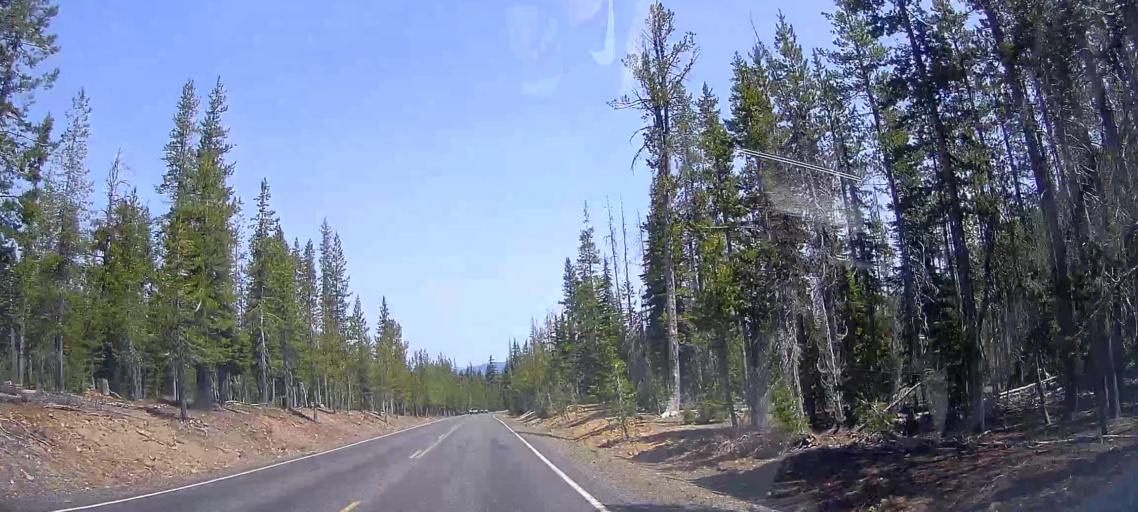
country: US
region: Oregon
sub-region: Jackson County
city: Shady Cove
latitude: 43.0028
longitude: -122.1342
